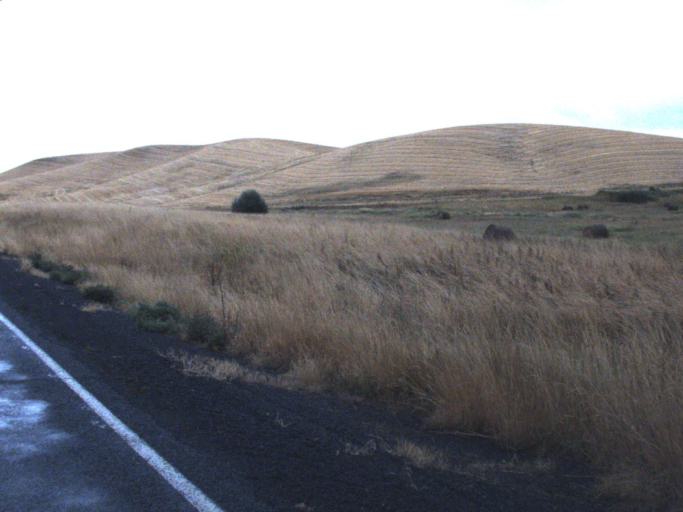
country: US
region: Washington
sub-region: Whitman County
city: Colfax
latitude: 47.0052
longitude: -117.3891
